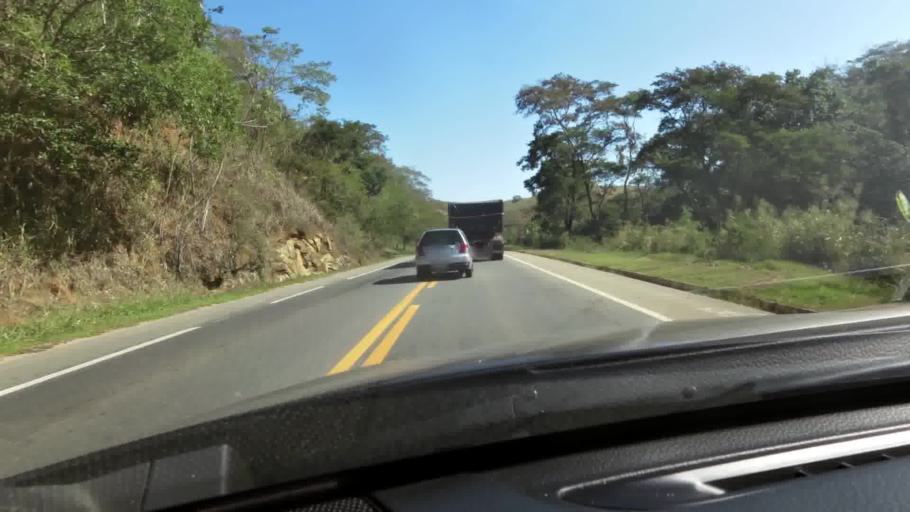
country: BR
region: Espirito Santo
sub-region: Cachoeiro De Itapemirim
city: Cachoeiro de Itapemirim
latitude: -20.8917
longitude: -41.0335
